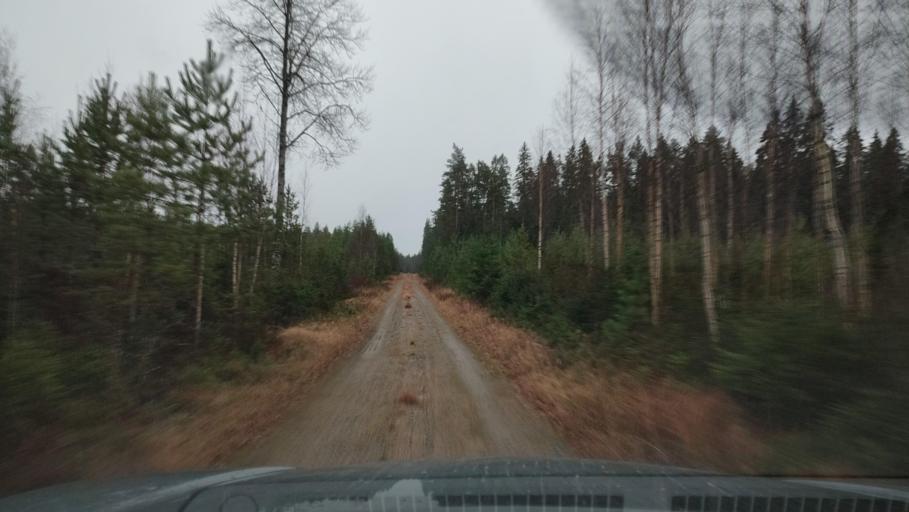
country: FI
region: Southern Ostrobothnia
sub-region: Suupohja
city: Karijoki
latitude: 62.1499
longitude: 21.5906
